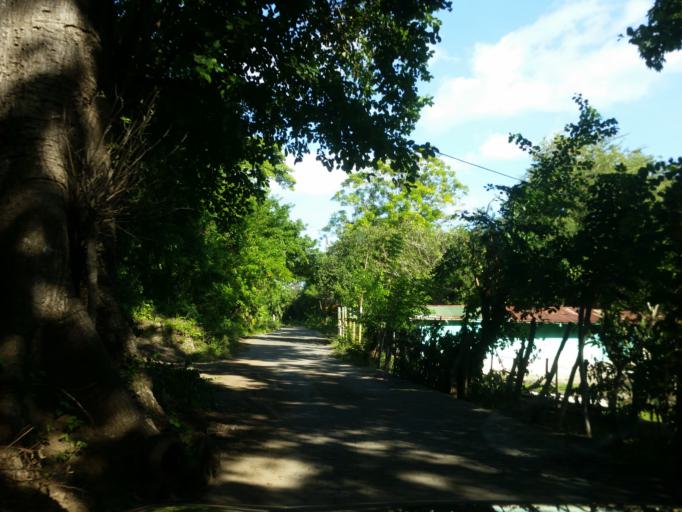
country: NI
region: Masaya
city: Catarina
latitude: 11.9409
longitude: -86.0488
